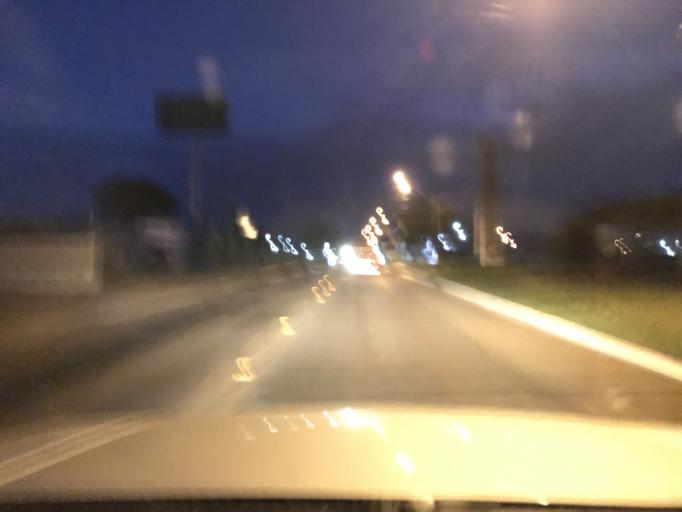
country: PY
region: Canindeyu
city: Salto del Guaira
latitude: -24.0956
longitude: -54.2388
